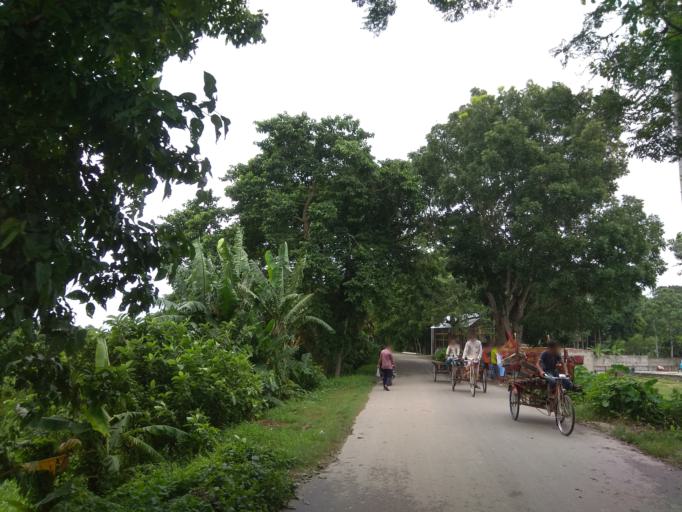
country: BD
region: Dhaka
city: Dohar
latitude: 23.4239
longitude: 90.0633
